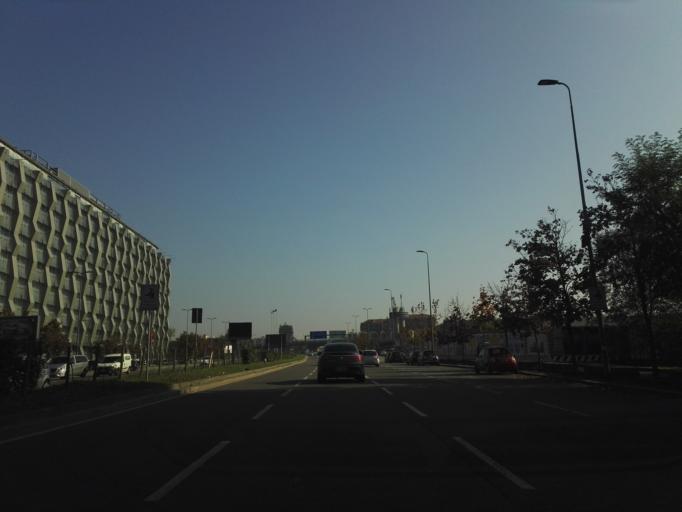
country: IT
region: Lombardy
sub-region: Citta metropolitana di Milano
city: Milano
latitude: 45.4374
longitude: 9.1656
